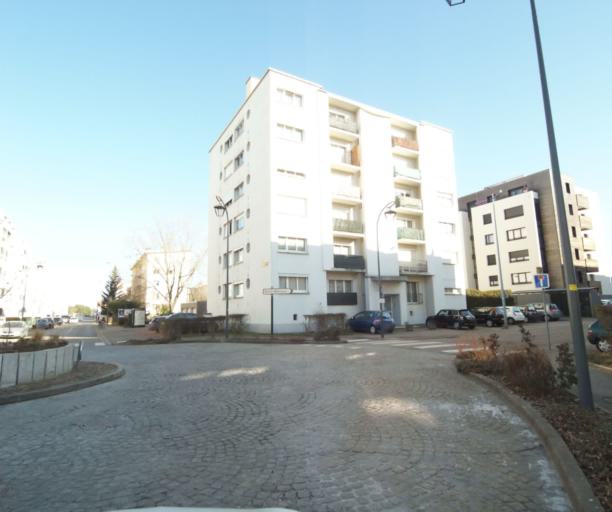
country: FR
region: Lorraine
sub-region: Departement de Meurthe-et-Moselle
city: Saint-Max
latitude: 48.6991
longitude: 6.2108
